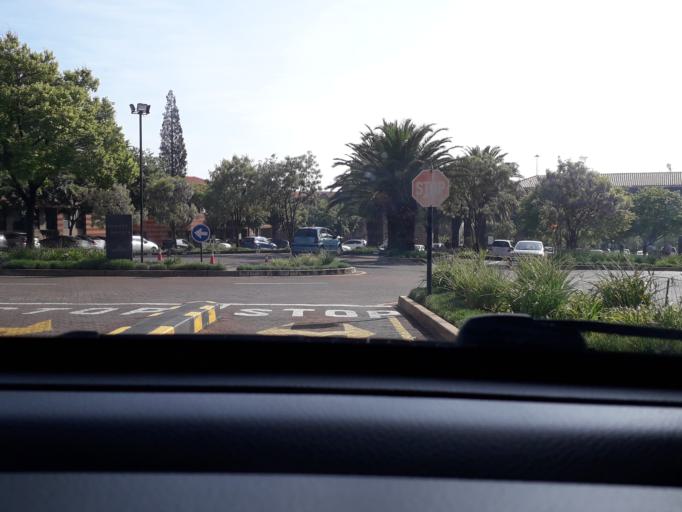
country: ZA
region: Gauteng
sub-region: Ekurhuleni Metropolitan Municipality
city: Germiston
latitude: -26.1740
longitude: 28.1283
